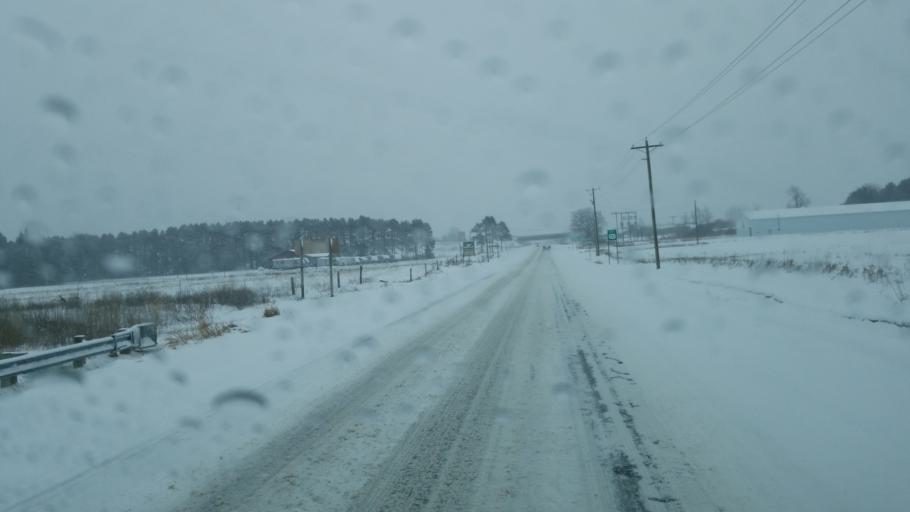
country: US
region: Michigan
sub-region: Mecosta County
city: Big Rapids
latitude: 43.5838
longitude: -85.4965
